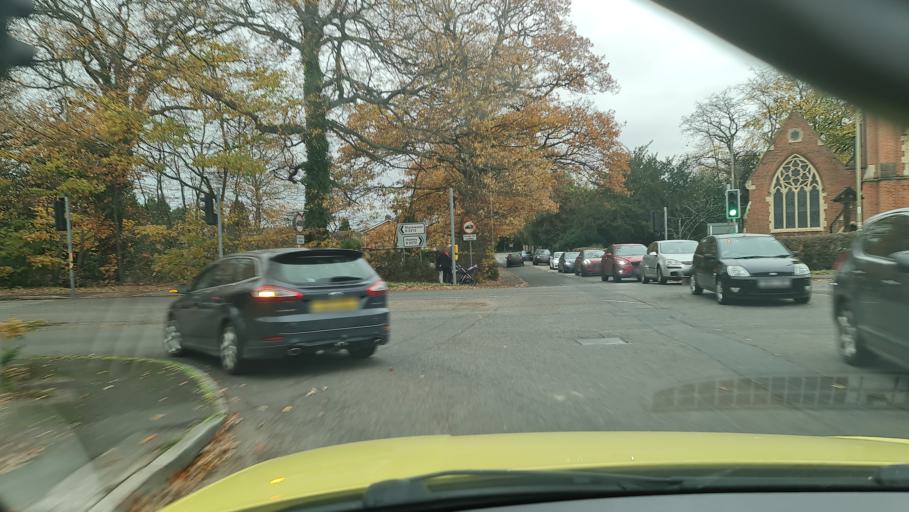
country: GB
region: England
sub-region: Bracknell Forest
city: Sandhurst
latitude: 51.3270
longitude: -0.7780
